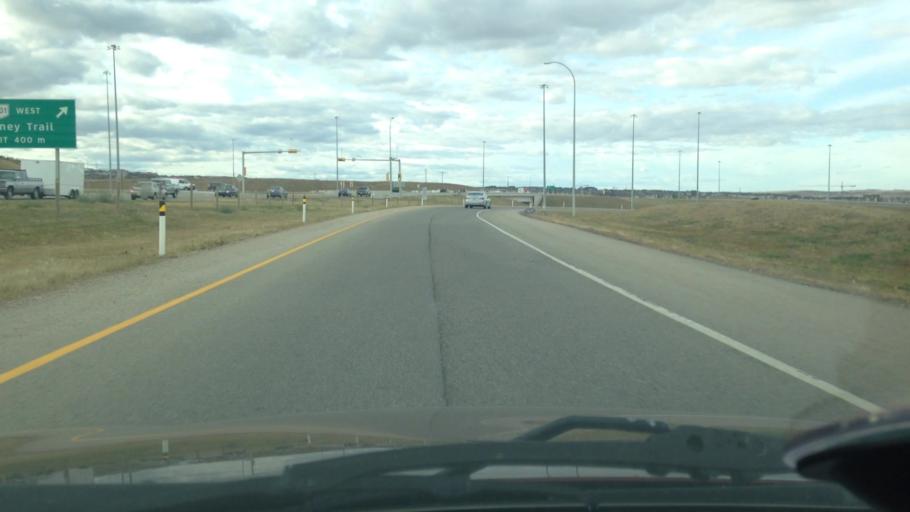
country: CA
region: Alberta
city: Calgary
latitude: 51.1497
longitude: -114.1384
